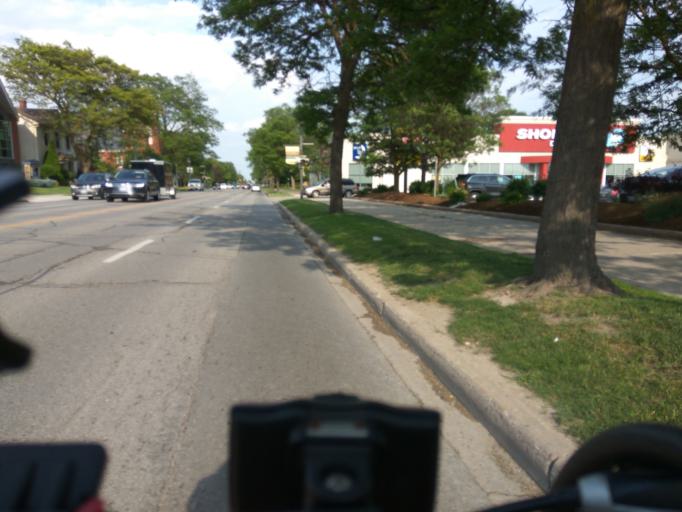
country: CA
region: Ontario
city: Stratford
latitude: 43.3713
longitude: -80.9785
